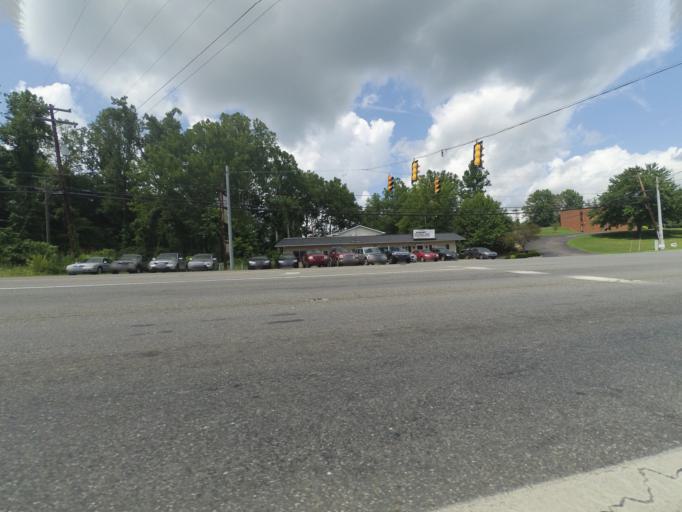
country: US
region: West Virginia
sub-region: Cabell County
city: Pea Ridge
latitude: 38.4105
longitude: -82.3276
